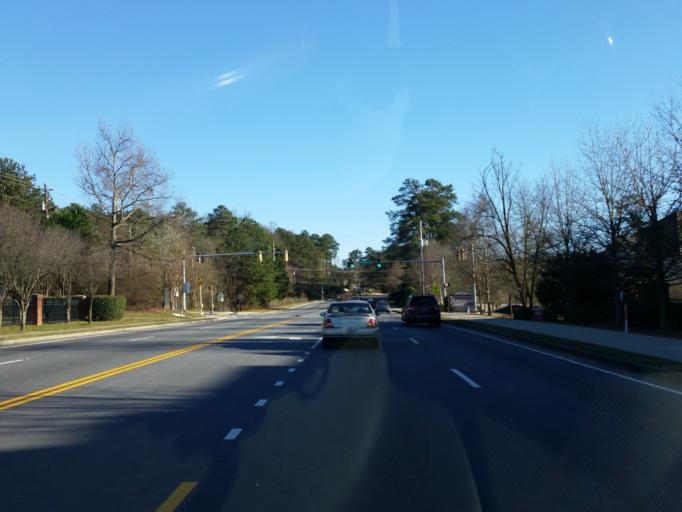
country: US
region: Georgia
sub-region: Cobb County
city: Smyrna
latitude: 33.8724
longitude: -84.4981
